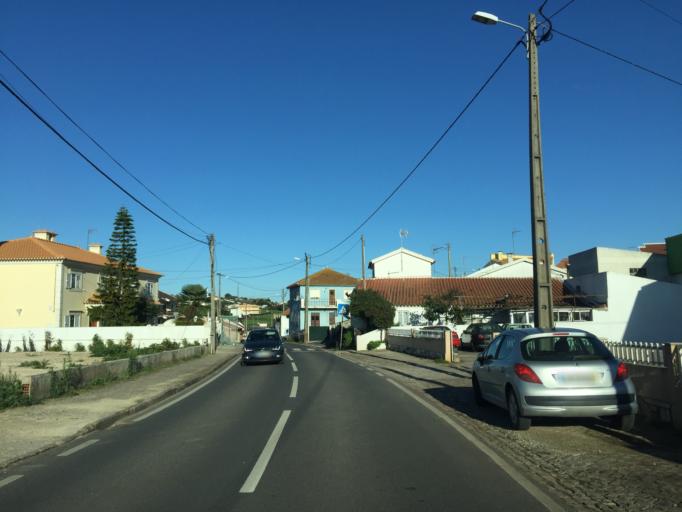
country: PT
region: Lisbon
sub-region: Sintra
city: Almargem
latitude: 38.8405
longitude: -9.2561
